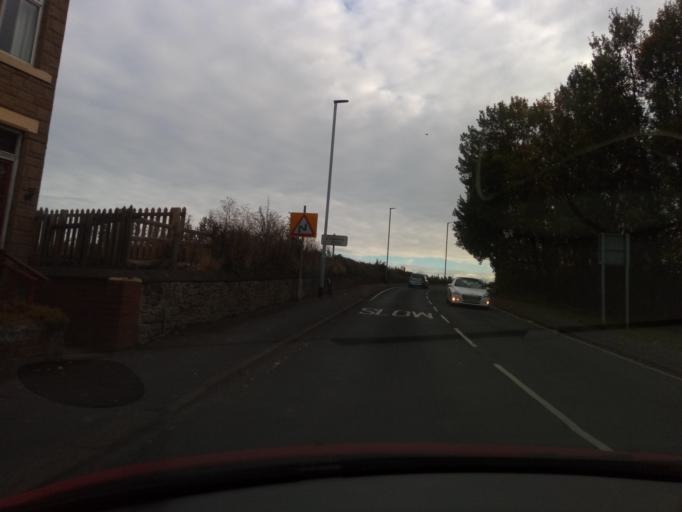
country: GB
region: England
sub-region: County Durham
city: Bishop Auckland
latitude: 54.6496
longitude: -1.6612
